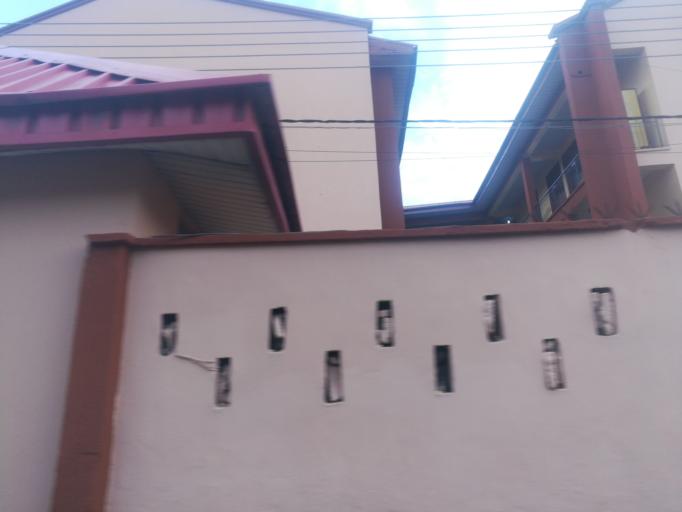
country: NG
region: Lagos
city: Ojota
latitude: 6.5633
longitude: 3.3731
